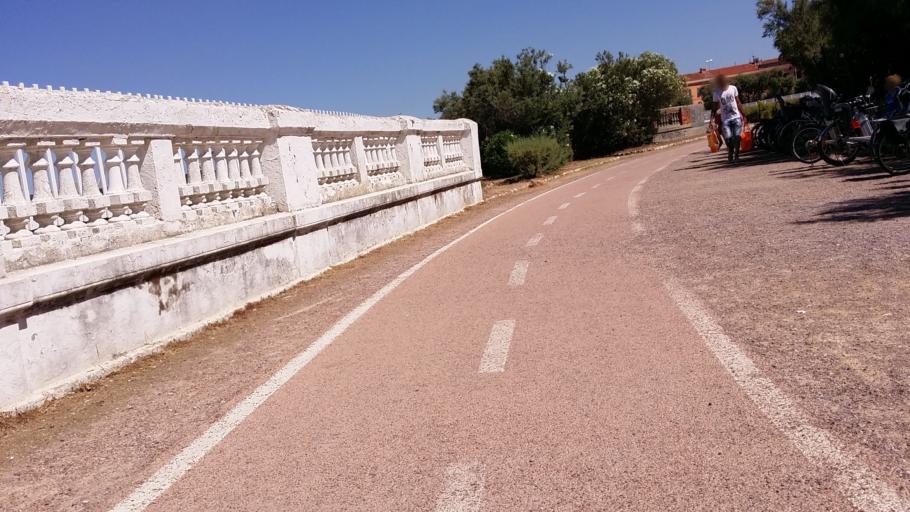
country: IT
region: Tuscany
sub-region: Provincia di Livorno
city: Livorno
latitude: 43.5142
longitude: 10.3157
